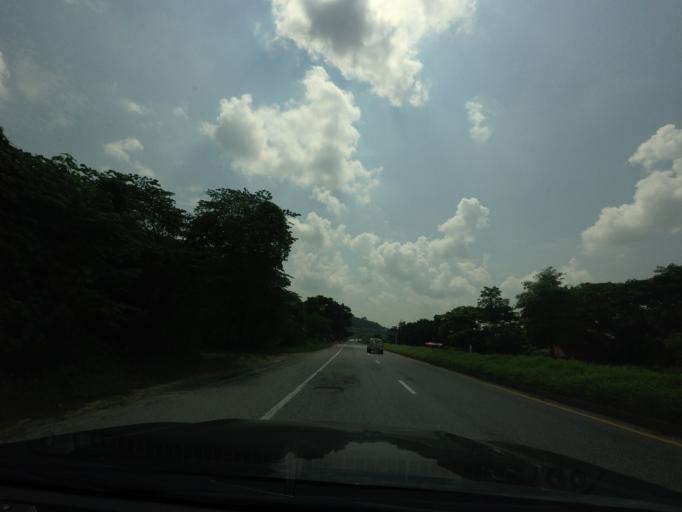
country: TH
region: Uttaradit
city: Lap Lae
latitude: 17.7908
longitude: 100.1172
